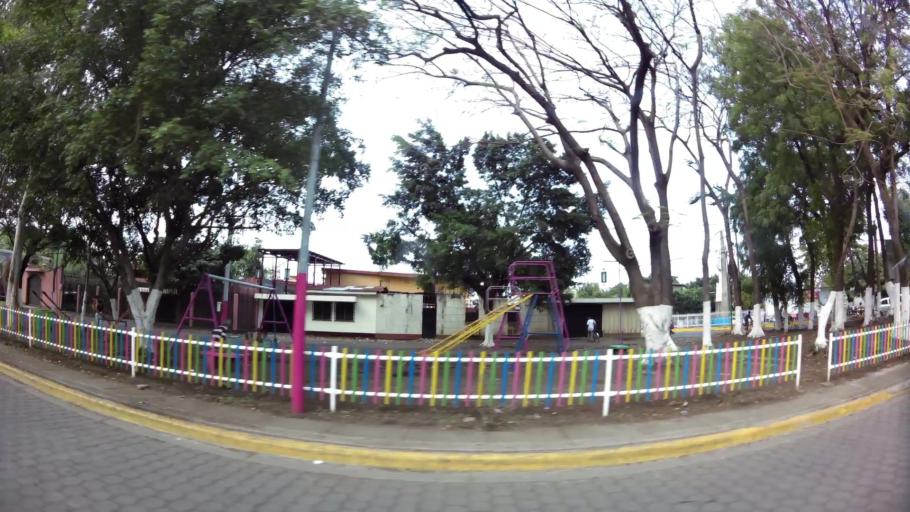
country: NI
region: Masaya
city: Masaya
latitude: 11.9825
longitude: -86.0973
